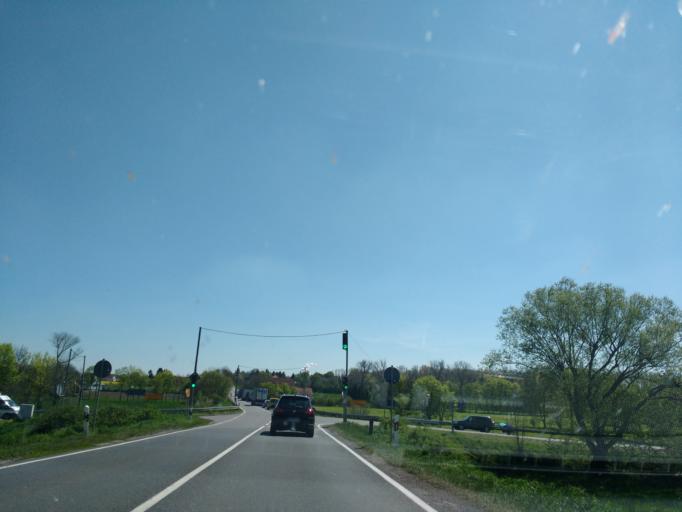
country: DE
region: Saxony-Anhalt
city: Deuben
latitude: 51.1323
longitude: 12.0544
